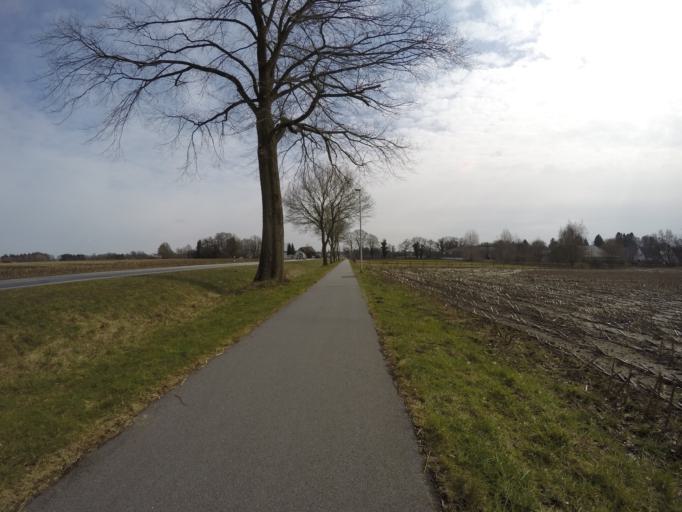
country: DE
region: Schleswig-Holstein
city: Quickborn
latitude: 53.7417
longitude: 9.8893
